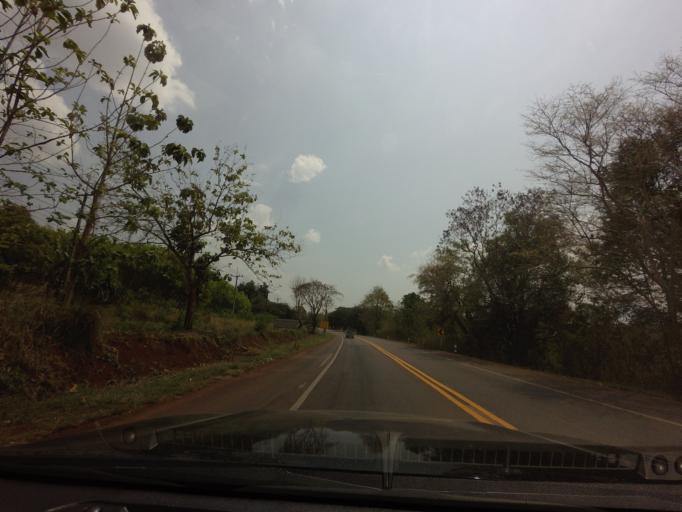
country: TH
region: Kanchanaburi
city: Sai Yok
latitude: 14.1383
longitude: 99.1496
